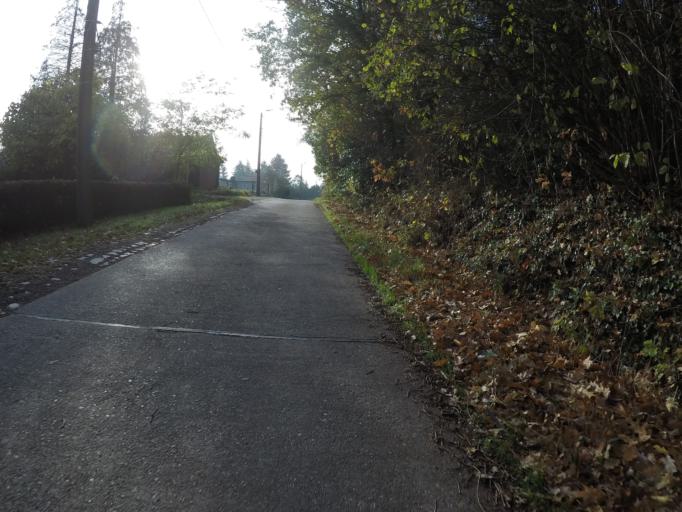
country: BE
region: Flanders
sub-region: Provincie Vlaams-Brabant
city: Begijnendijk
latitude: 51.0036
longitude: 4.7699
